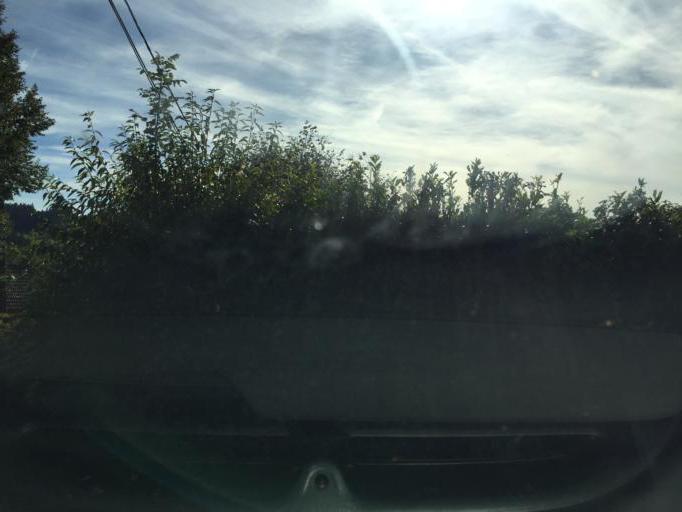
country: FR
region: Rhone-Alpes
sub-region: Departement de la Loire
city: Belmont-de-la-Loire
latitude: 46.1929
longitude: 4.4174
